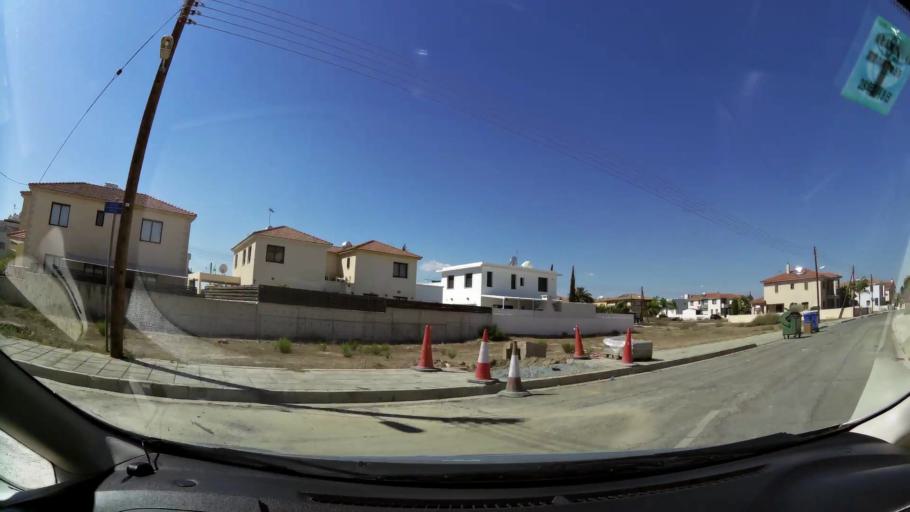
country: CY
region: Larnaka
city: Livadia
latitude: 34.9592
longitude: 33.6404
